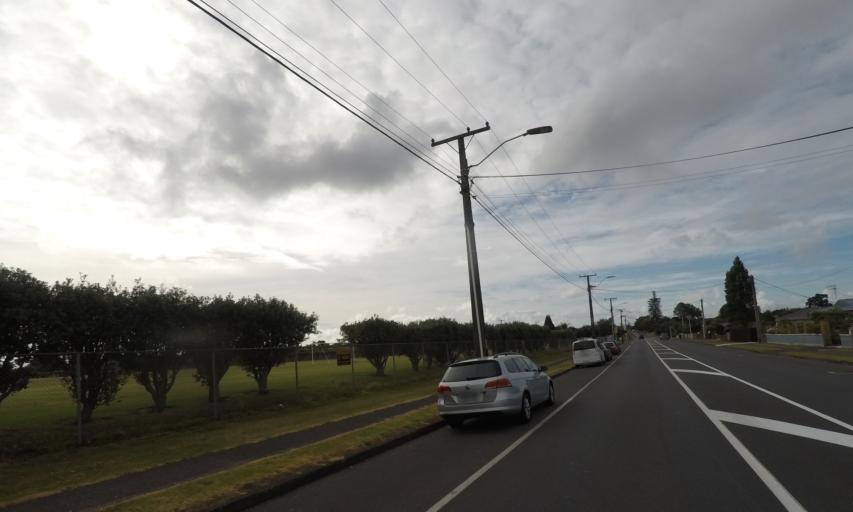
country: NZ
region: Northland
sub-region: Whangarei
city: Whangarei
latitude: -35.6858
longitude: 174.3023
